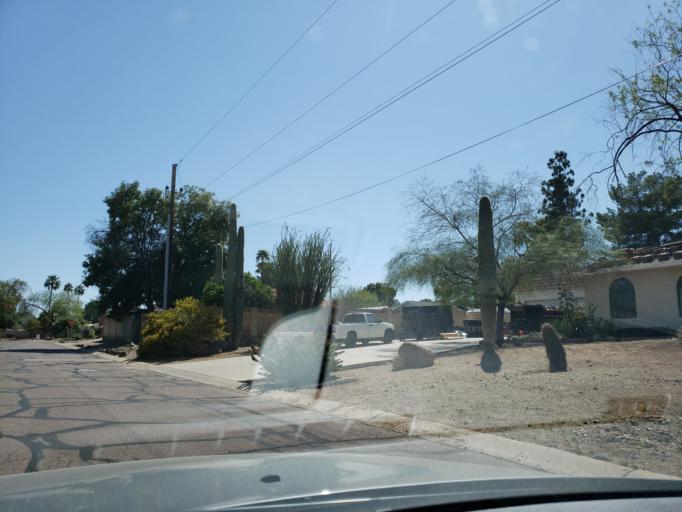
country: US
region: Arizona
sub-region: Maricopa County
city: Paradise Valley
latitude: 33.5903
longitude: -112.0272
